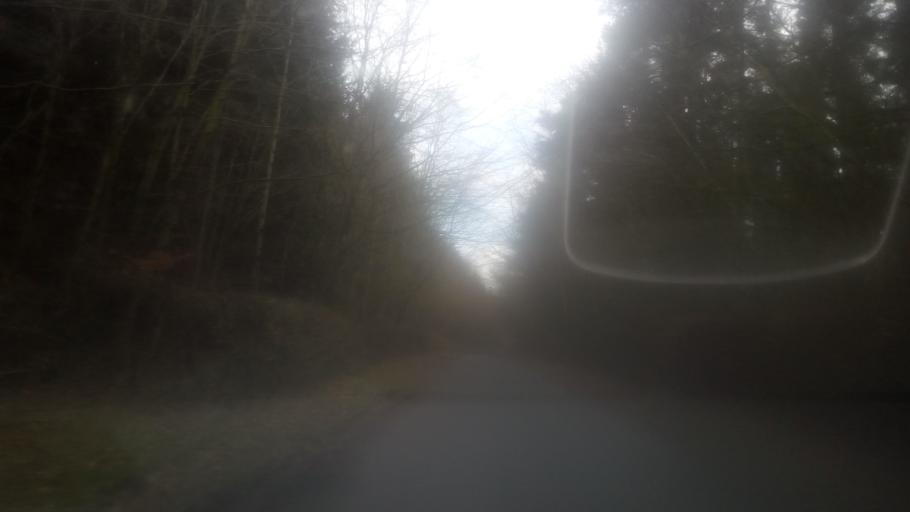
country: GB
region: Scotland
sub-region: The Scottish Borders
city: Jedburgh
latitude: 55.4813
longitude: -2.5241
